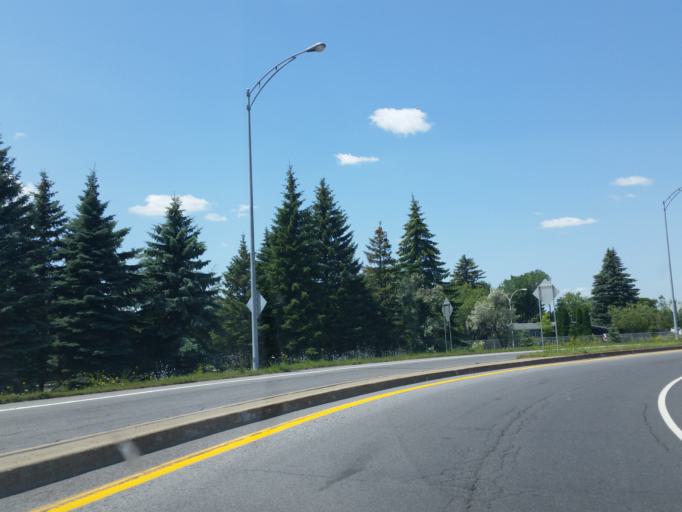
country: CA
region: Quebec
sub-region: Monteregie
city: Saint-Jean-sur-Richelieu
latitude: 45.3255
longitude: -73.2710
